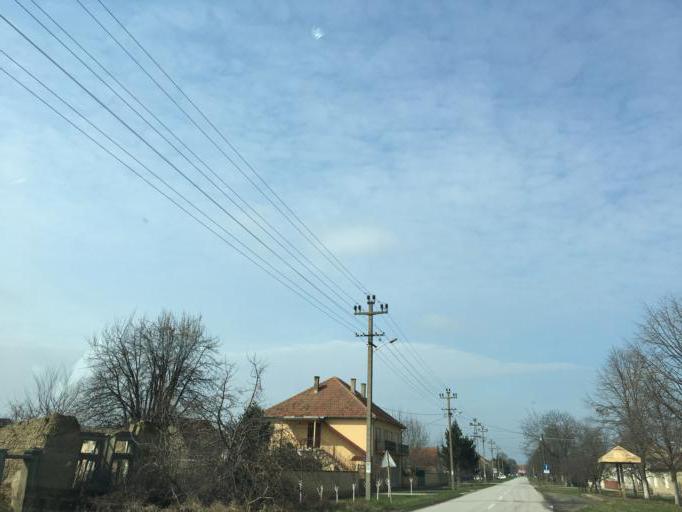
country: RS
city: Centa
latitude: 45.1039
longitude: 20.3941
